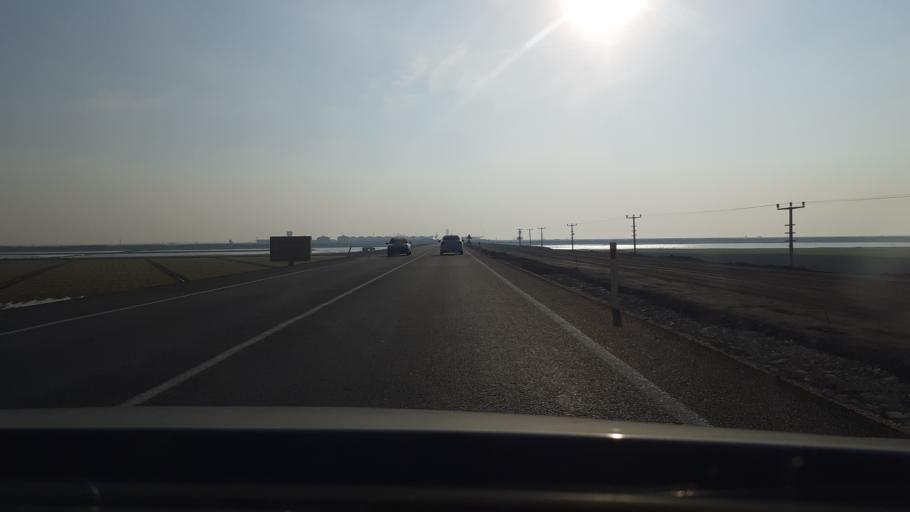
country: TR
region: Hatay
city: Serinyol
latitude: 36.3678
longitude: 36.2620
